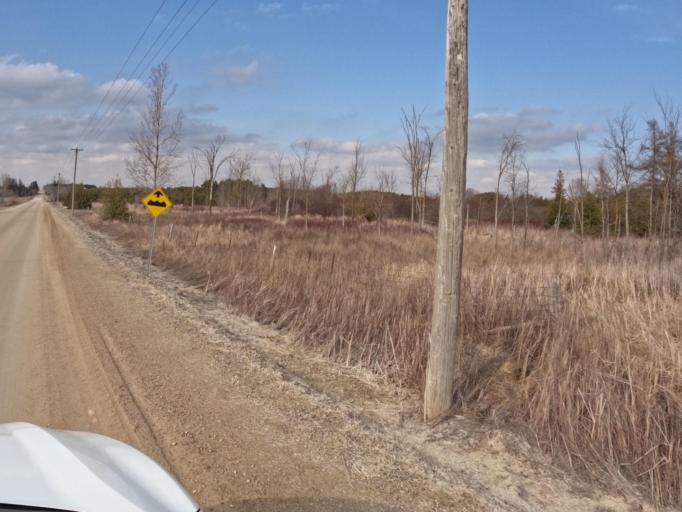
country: CA
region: Ontario
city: Orangeville
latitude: 43.8905
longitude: -80.2991
